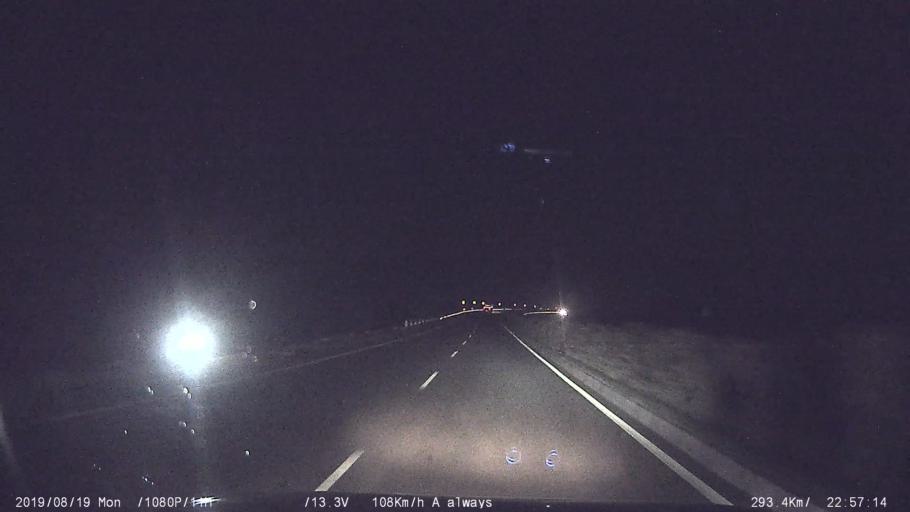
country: IN
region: Tamil Nadu
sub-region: Erode
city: Perundurai
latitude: 11.2809
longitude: 77.5573
